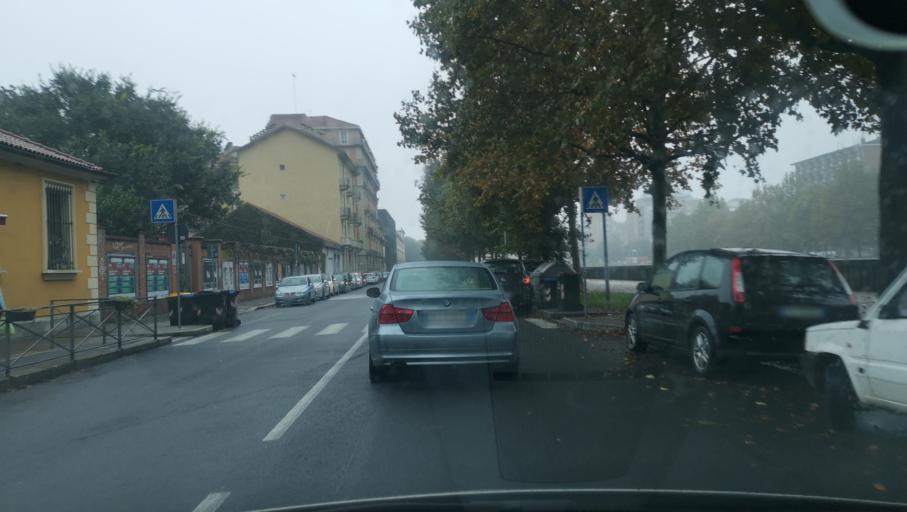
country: IT
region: Piedmont
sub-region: Provincia di Torino
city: Turin
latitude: 45.0788
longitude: 7.6901
